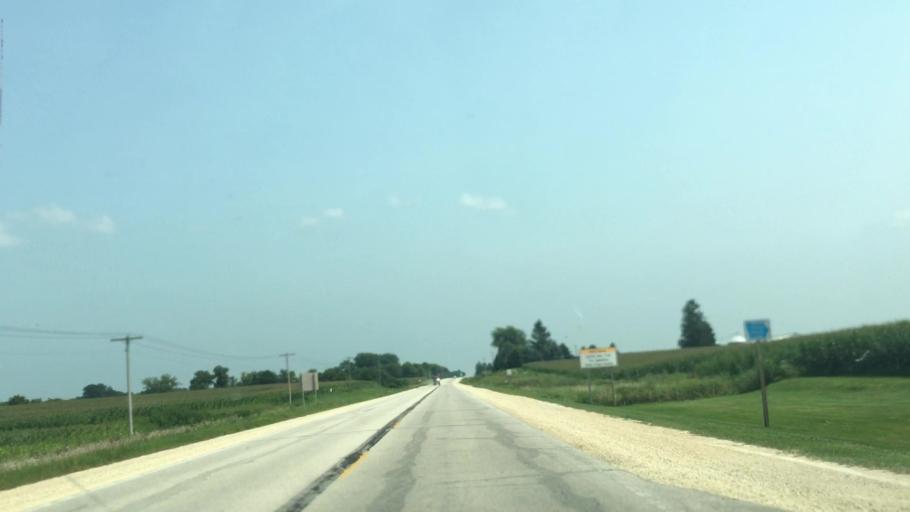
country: US
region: Iowa
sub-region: Fayette County
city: Oelwein
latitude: 42.6793
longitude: -91.8886
